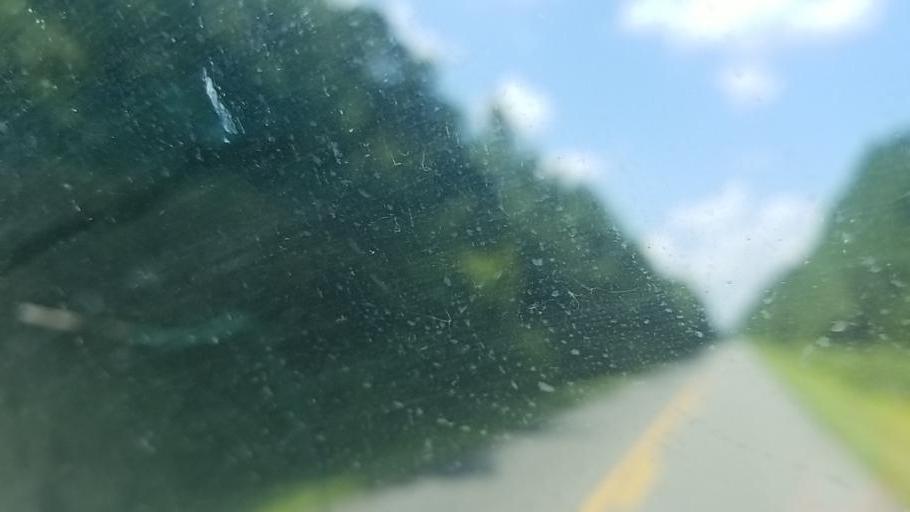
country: US
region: Maryland
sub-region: Wicomico County
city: Hebron
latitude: 38.4425
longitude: -75.8460
